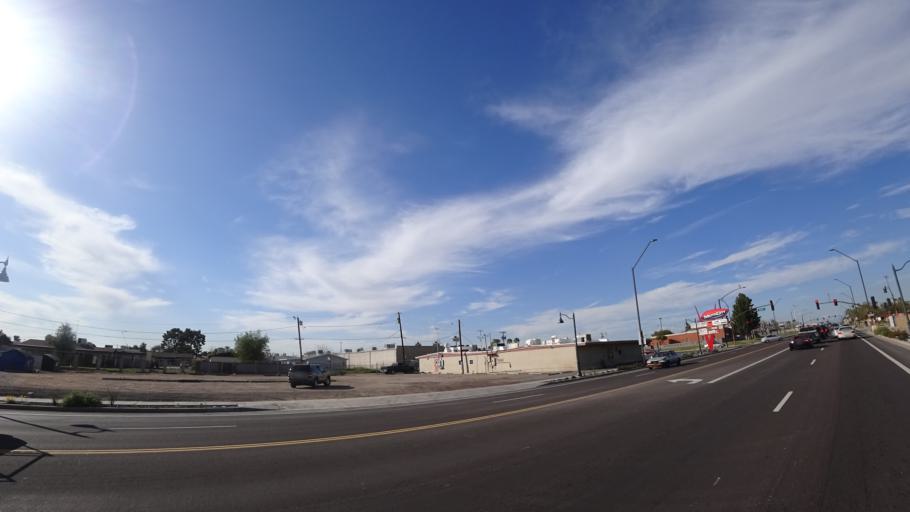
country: US
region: Arizona
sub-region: Maricopa County
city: Avondale
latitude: 33.4381
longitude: -112.3410
